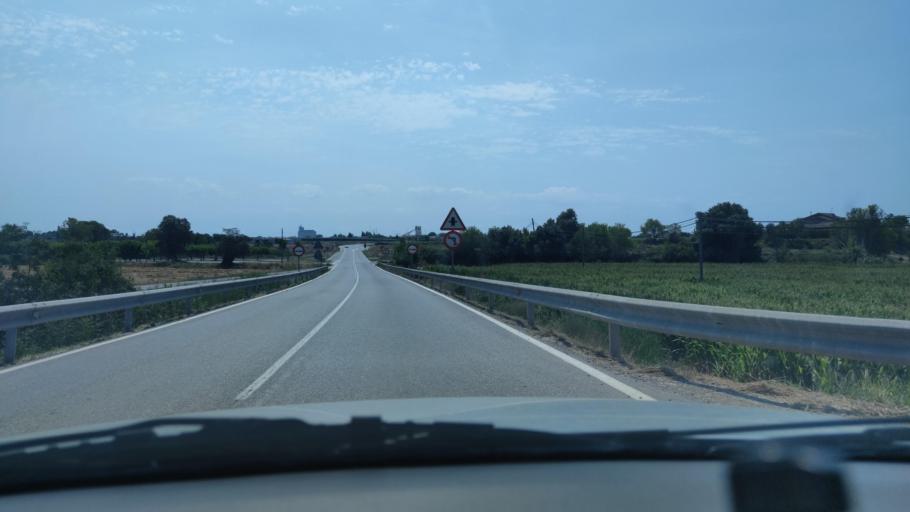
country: ES
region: Catalonia
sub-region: Provincia de Lleida
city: Bellpuig
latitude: 41.6478
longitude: 0.9978
